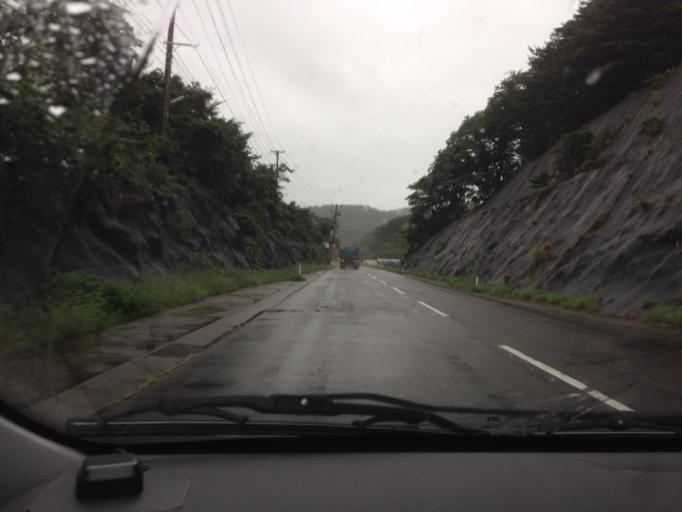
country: JP
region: Fukushima
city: Koriyama
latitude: 37.4234
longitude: 140.2738
